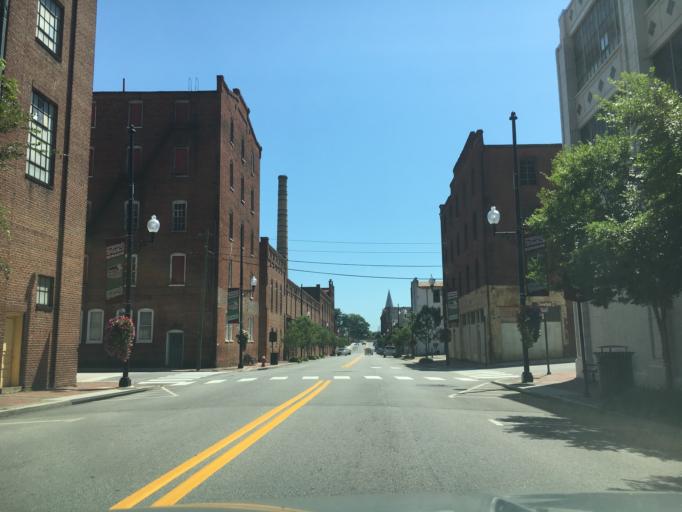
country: US
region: Virginia
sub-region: City of Danville
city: Danville
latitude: 36.5862
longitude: -79.3883
